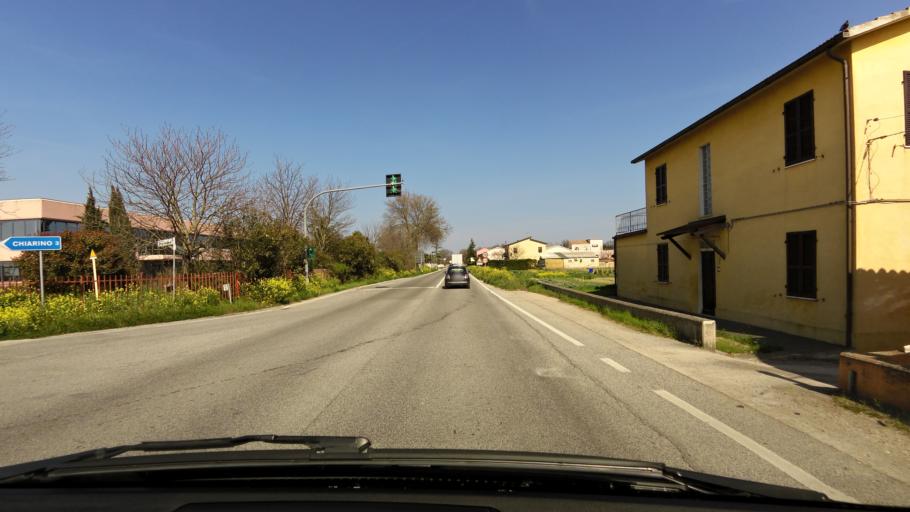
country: IT
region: The Marches
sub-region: Provincia di Macerata
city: Potenza Picena
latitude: 43.3801
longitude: 13.6083
